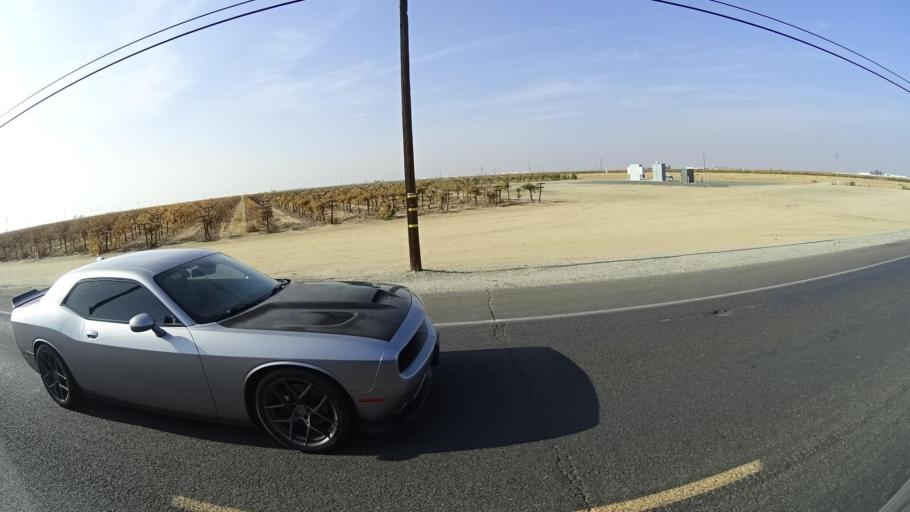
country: US
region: California
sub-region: Tulare County
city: Richgrove
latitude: 35.7848
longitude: -119.1184
